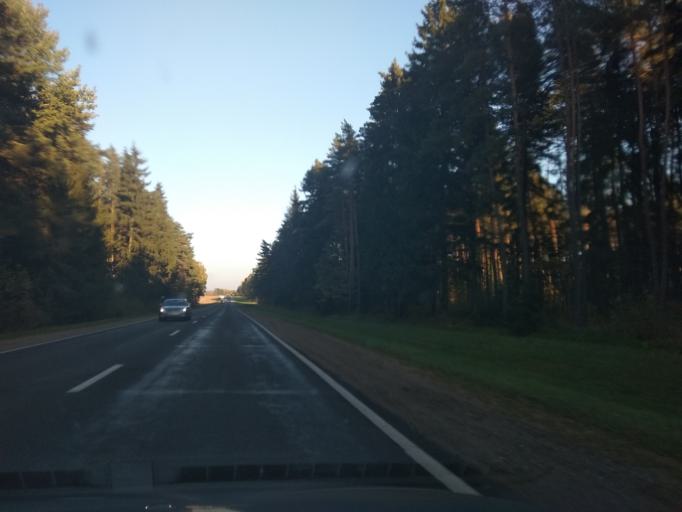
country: BY
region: Grodnenskaya
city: Vawkavysk
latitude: 53.1485
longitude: 24.5378
